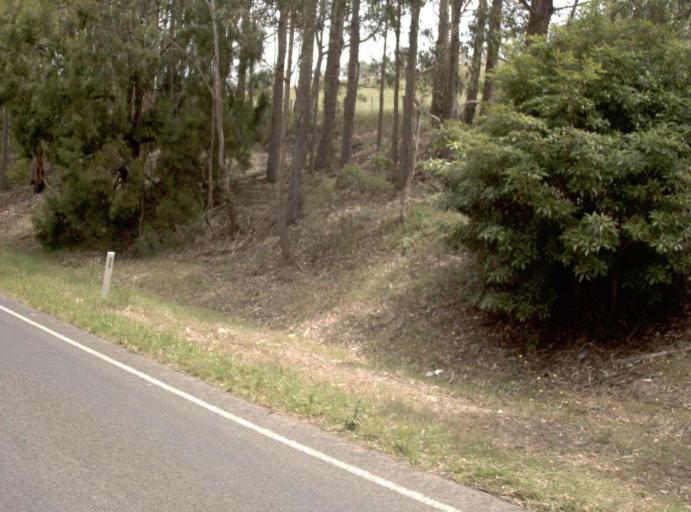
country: AU
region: Victoria
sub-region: Latrobe
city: Traralgon
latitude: -38.4615
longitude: 146.7235
